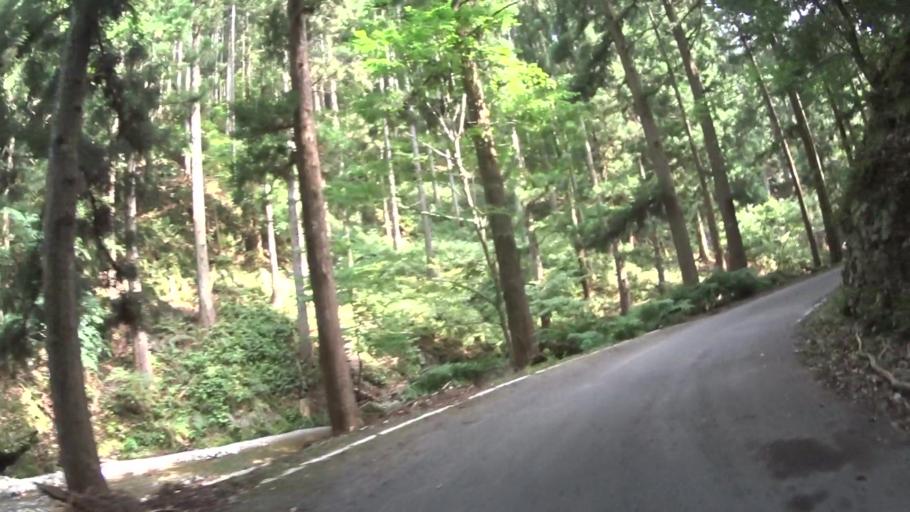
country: JP
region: Fukui
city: Obama
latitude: 35.2826
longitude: 135.6427
